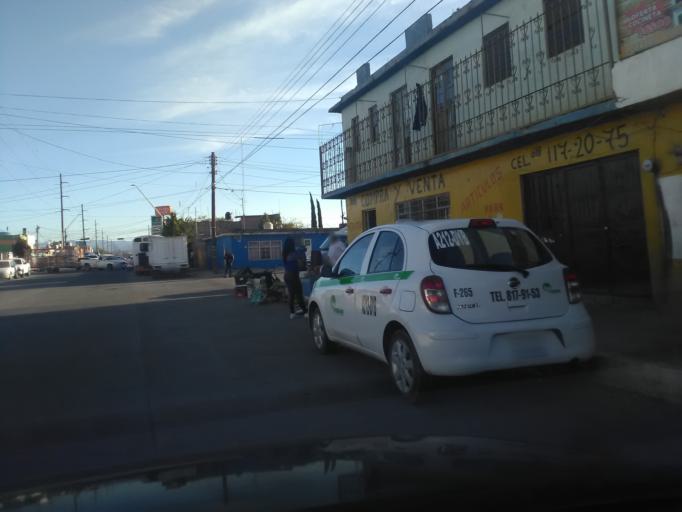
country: MX
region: Durango
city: Victoria de Durango
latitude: 24.0213
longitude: -104.6329
